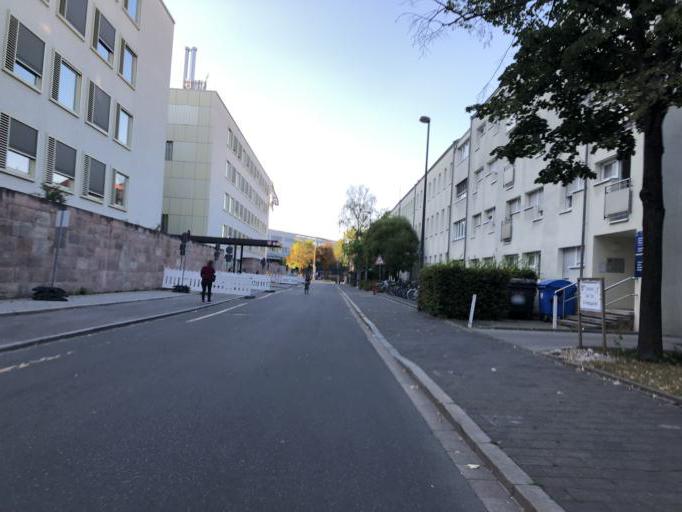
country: DE
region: Bavaria
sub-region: Regierungsbezirk Mittelfranken
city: Erlangen
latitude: 49.5991
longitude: 11.0126
